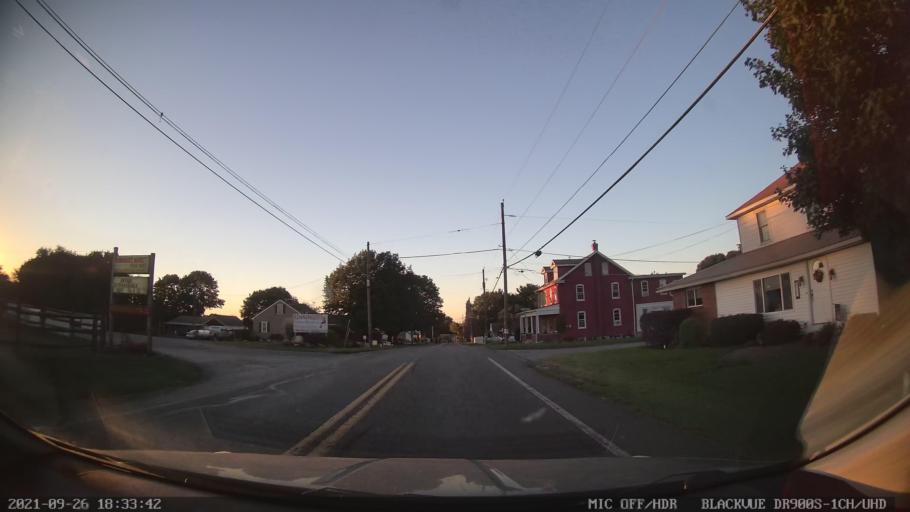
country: US
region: Pennsylvania
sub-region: Berks County
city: Kutztown
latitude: 40.5037
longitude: -75.7682
